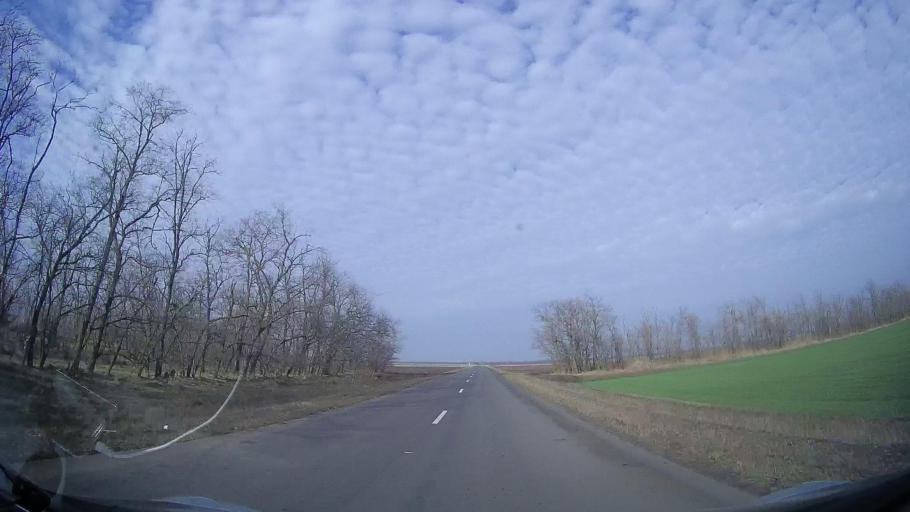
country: RU
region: Rostov
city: Gigant
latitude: 46.8768
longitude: 41.2717
